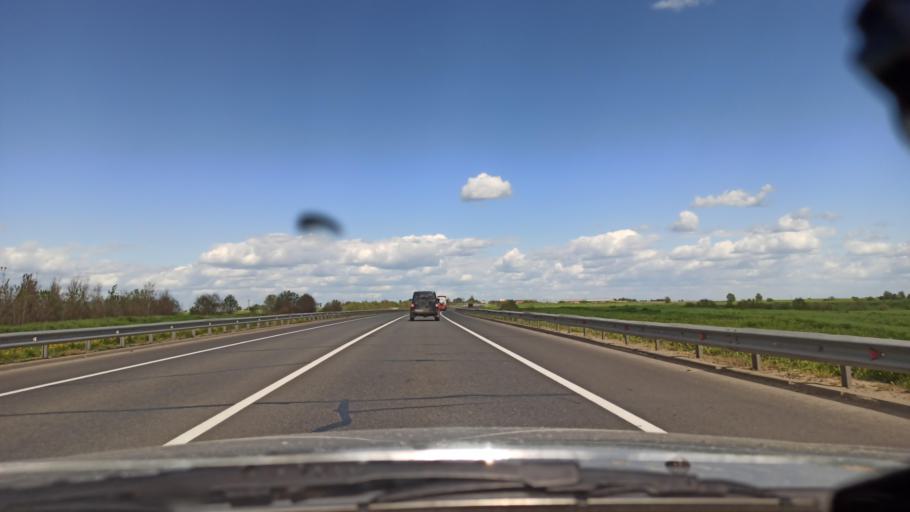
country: RU
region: Vologda
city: Vologda
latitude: 59.2759
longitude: 39.8163
